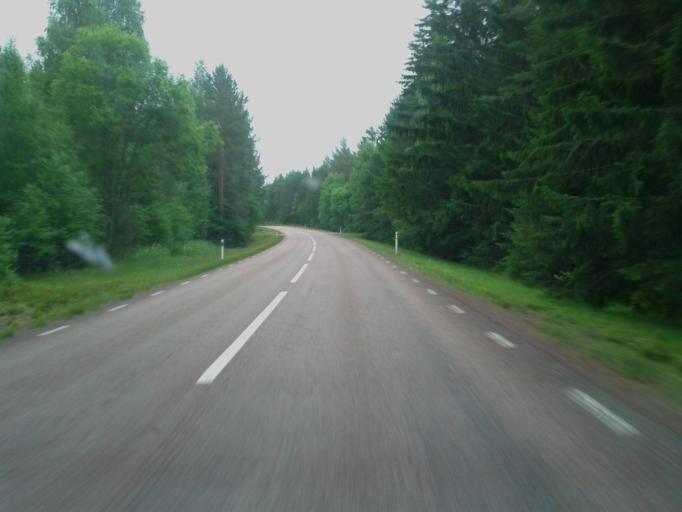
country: SE
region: Dalarna
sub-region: Mora Kommun
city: Mora
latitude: 61.0898
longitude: 14.3072
